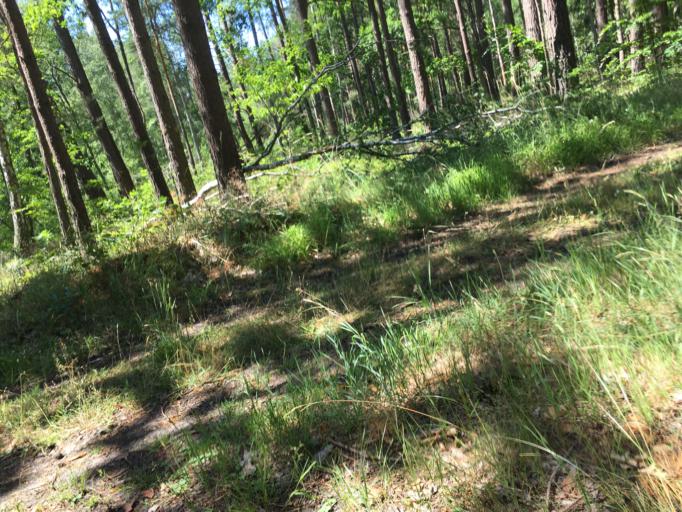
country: DE
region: Brandenburg
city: Marienwerder
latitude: 52.9180
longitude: 13.5825
